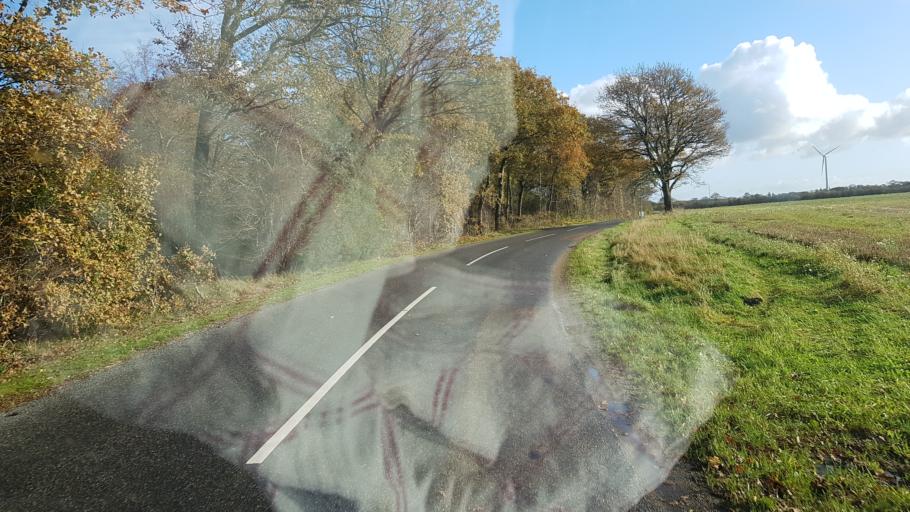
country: DK
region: South Denmark
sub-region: Varde Kommune
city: Olgod
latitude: 55.6912
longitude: 8.6691
